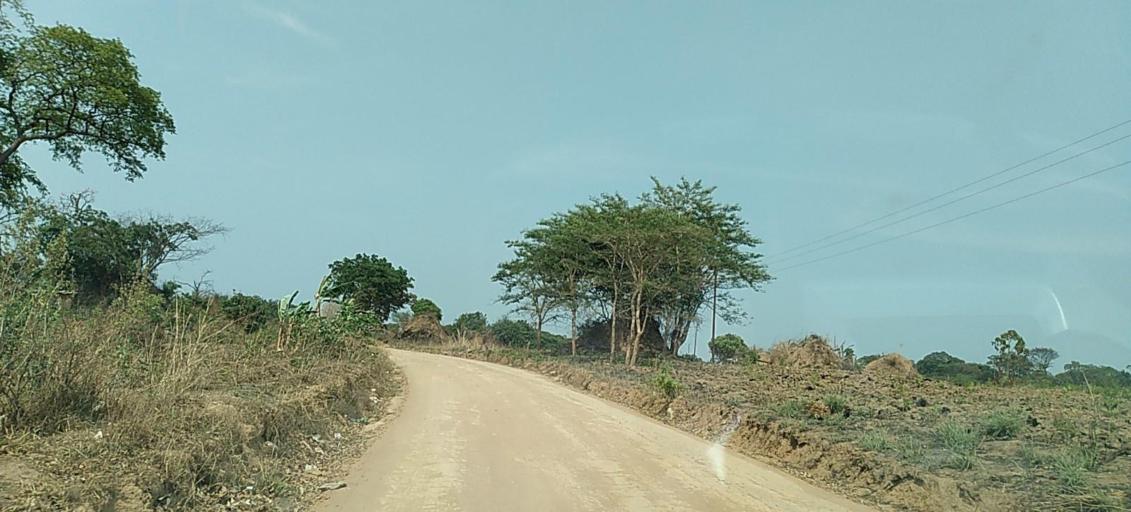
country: ZM
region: Copperbelt
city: Chililabombwe
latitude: -12.3377
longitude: 27.7215
